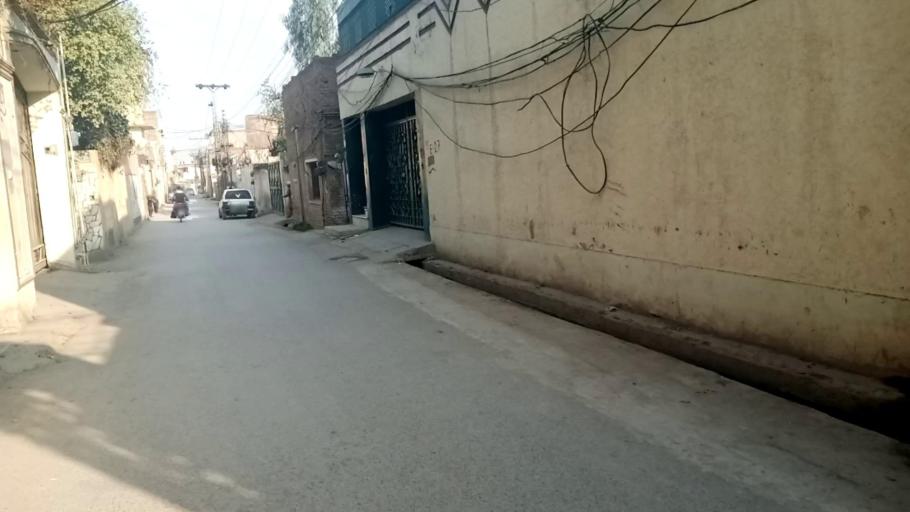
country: PK
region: Khyber Pakhtunkhwa
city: Peshawar
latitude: 34.0027
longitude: 71.4704
